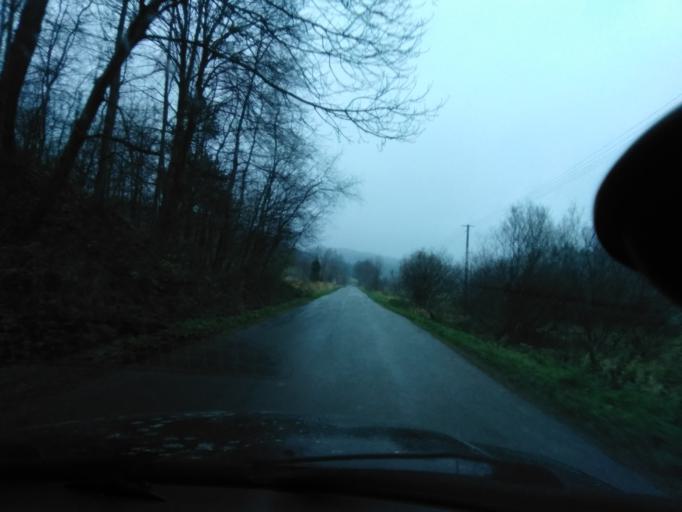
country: PL
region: Subcarpathian Voivodeship
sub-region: Powiat brzozowski
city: Jablonka
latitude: 49.7393
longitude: 22.1504
